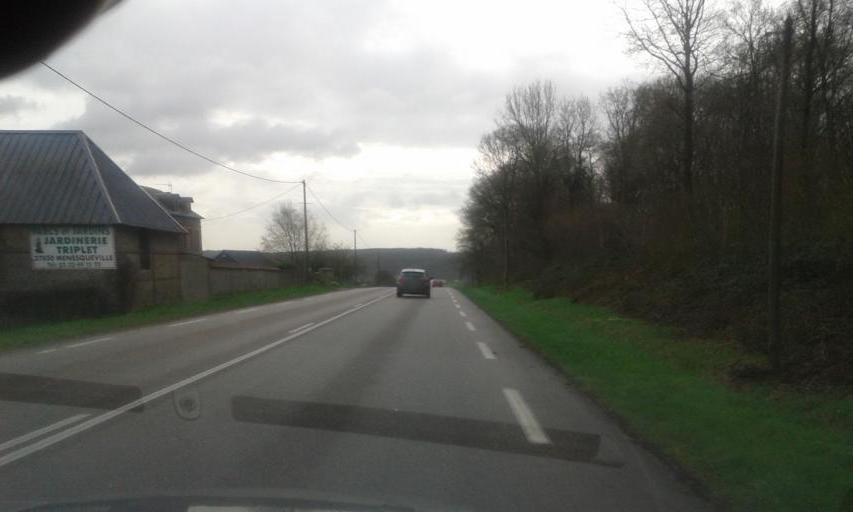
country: FR
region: Haute-Normandie
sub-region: Departement de l'Eure
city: Fleury-sur-Andelle
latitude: 49.3713
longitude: 1.3370
